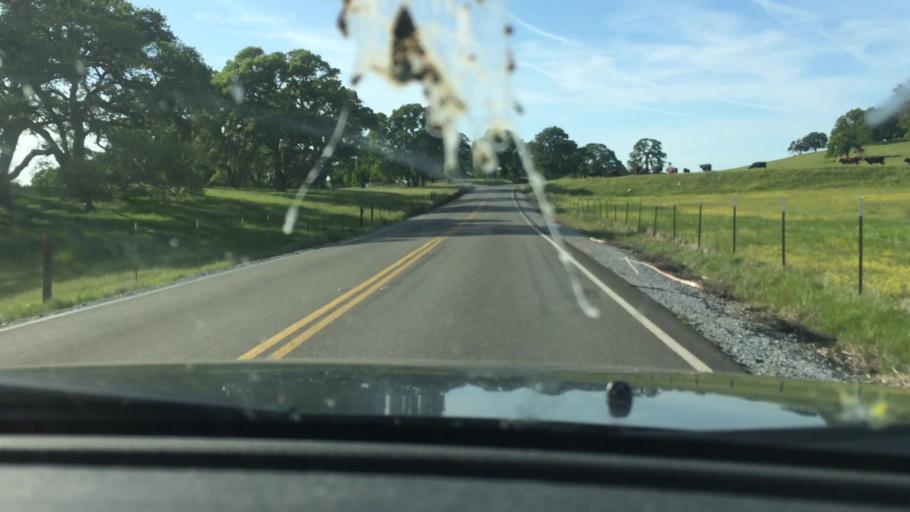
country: US
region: California
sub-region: Amador County
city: Plymouth
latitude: 38.4979
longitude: -120.9393
